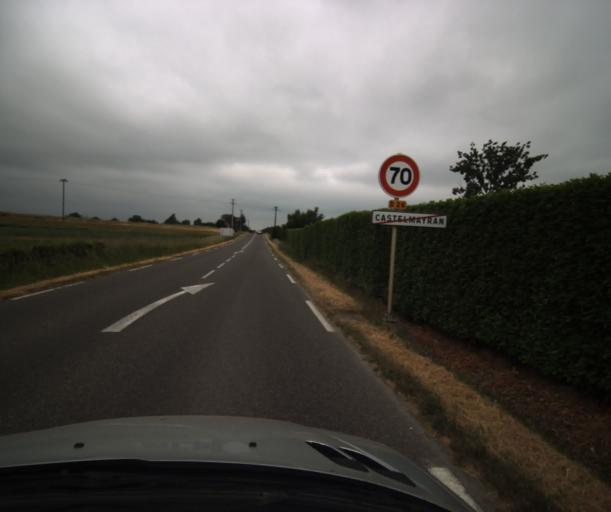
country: FR
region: Midi-Pyrenees
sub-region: Departement du Tarn-et-Garonne
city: Saint-Nicolas-de-la-Grave
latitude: 44.0326
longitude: 1.0382
